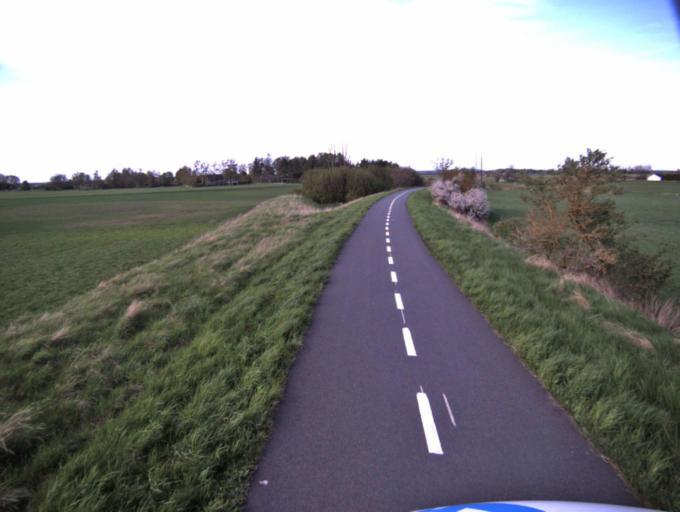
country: SE
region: Skane
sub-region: Kristianstads Kommun
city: Kristianstad
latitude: 56.0143
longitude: 14.0845
